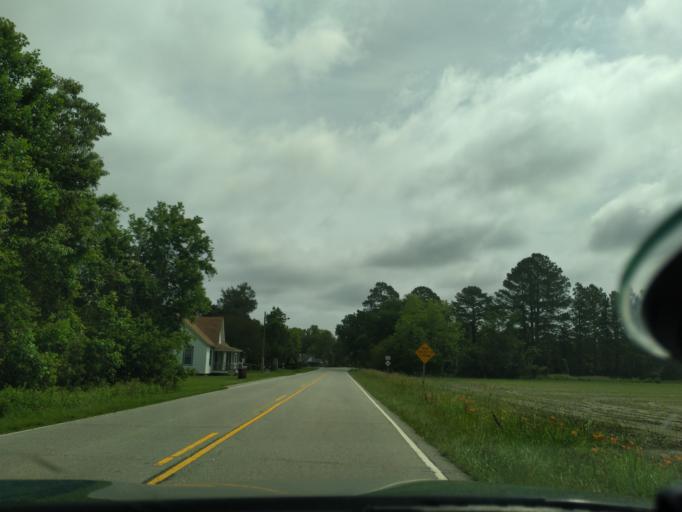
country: US
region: North Carolina
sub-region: Chowan County
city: Edenton
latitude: 35.9238
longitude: -76.5924
